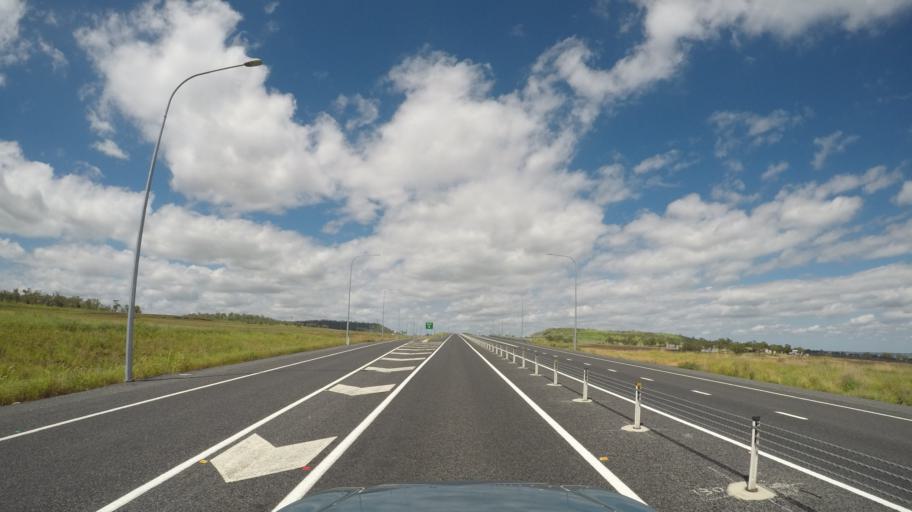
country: AU
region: Queensland
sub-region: Toowoomba
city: Westbrook
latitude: -27.5435
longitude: 151.8382
